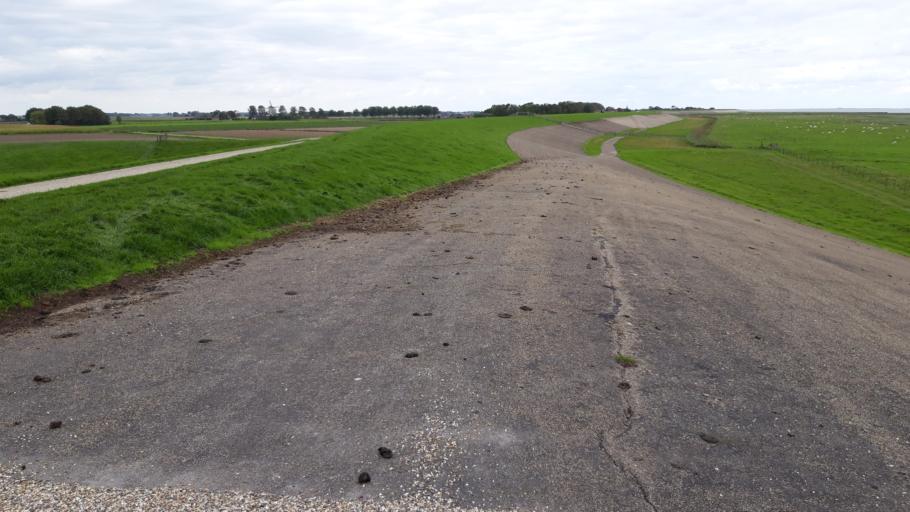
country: NL
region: Friesland
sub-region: Gemeente Dongeradeel
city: Anjum
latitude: 53.4006
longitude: 6.1009
